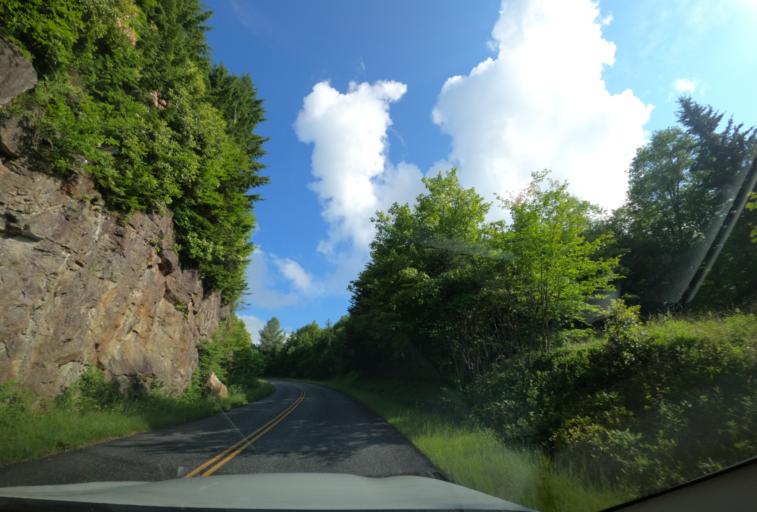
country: US
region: North Carolina
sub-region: Haywood County
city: Hazelwood
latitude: 35.3427
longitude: -82.9712
